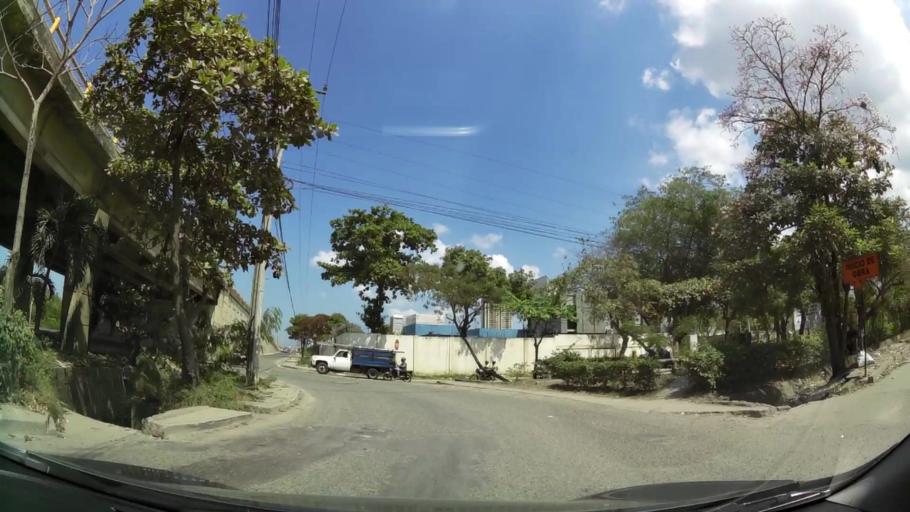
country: CO
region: Bolivar
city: Cartagena
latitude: 10.3729
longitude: -75.5052
